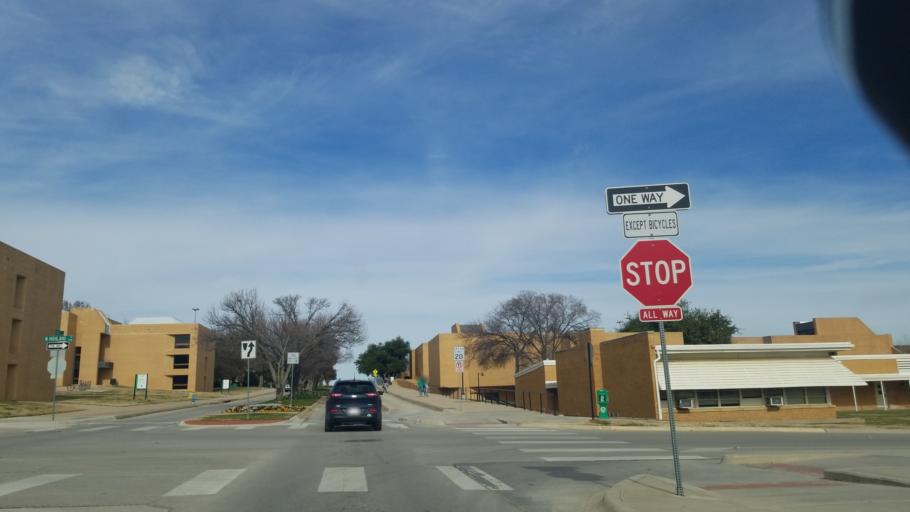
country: US
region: Texas
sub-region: Denton County
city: Denton
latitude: 33.2092
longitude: -97.1507
